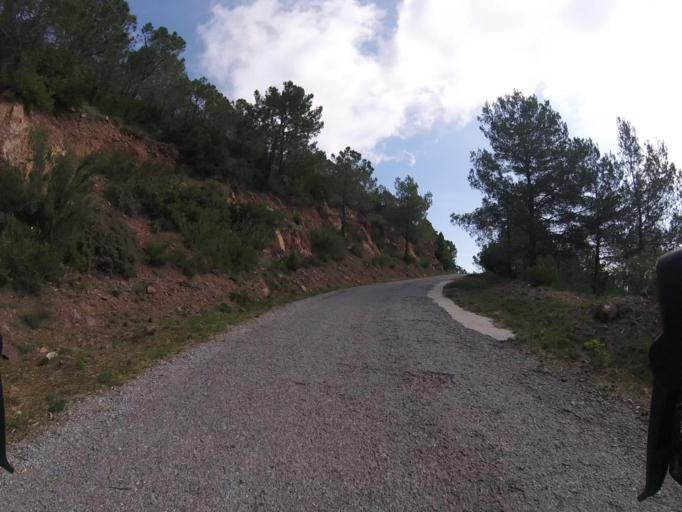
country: ES
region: Valencia
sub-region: Provincia de Castello
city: Benicassim
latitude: 40.0776
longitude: 0.0215
